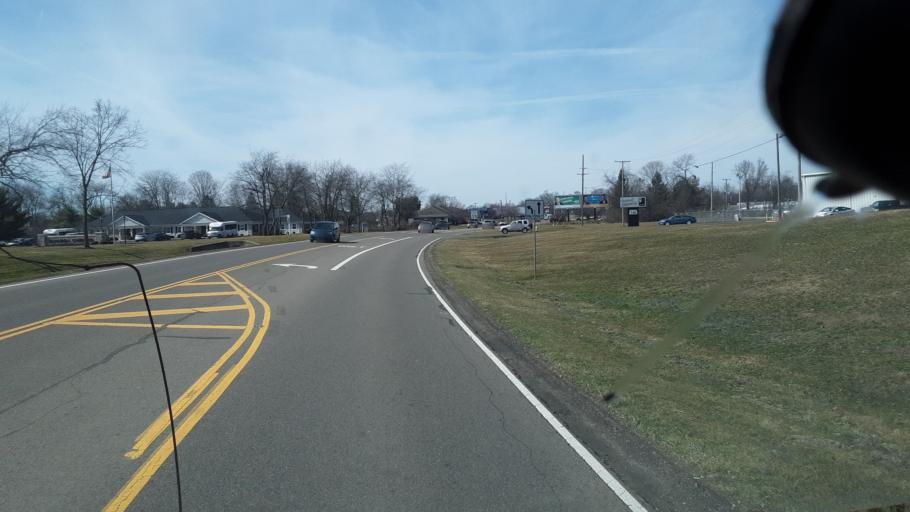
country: US
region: Ohio
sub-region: Licking County
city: Heath
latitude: 40.0353
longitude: -82.4229
